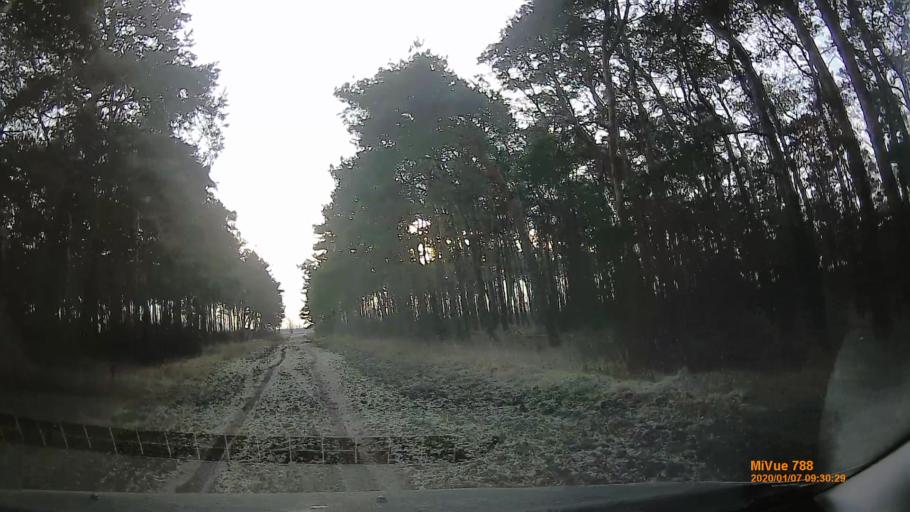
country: HU
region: Gyor-Moson-Sopron
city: Rajka
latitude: 47.9475
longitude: 17.1721
